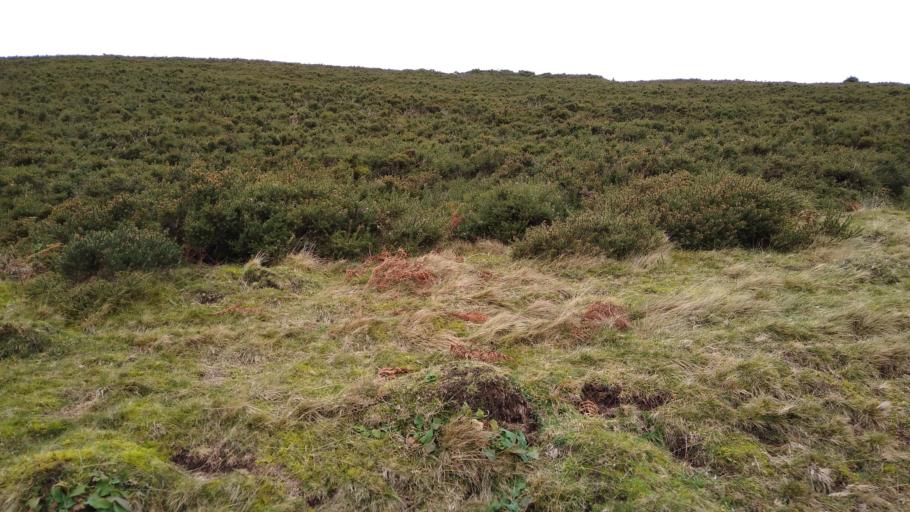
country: GB
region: England
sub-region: Cumbria
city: Keswick
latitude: 54.6534
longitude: -3.2371
